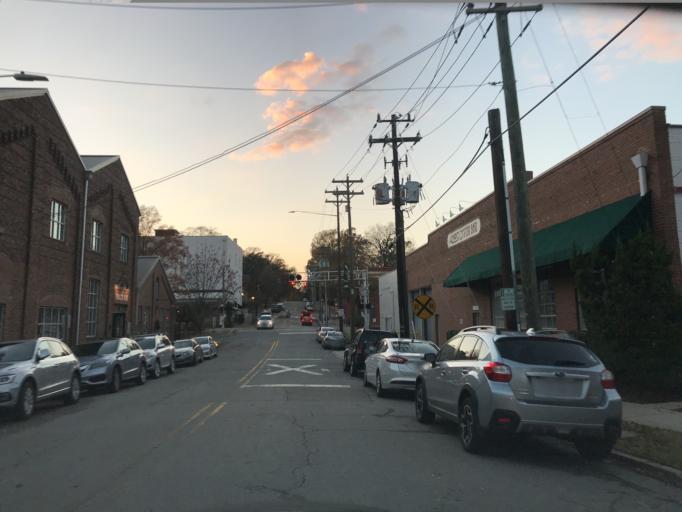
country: US
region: North Carolina
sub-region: Wake County
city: Raleigh
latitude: 35.7828
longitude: -78.6460
